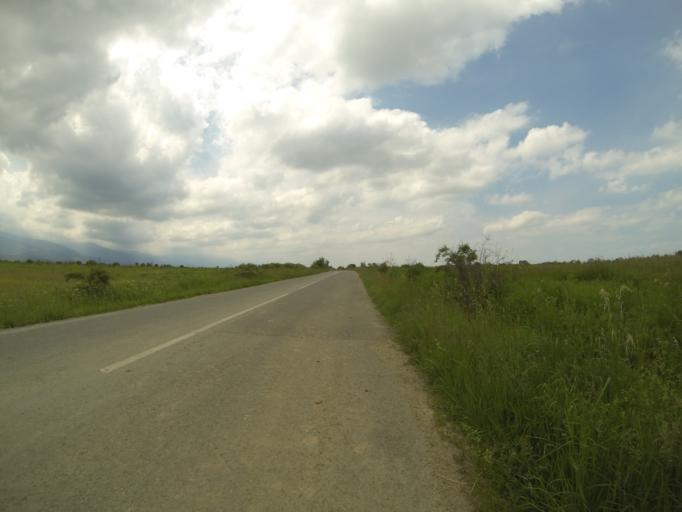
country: RO
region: Brasov
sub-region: Comuna Harseni
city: Harseni
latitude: 45.7360
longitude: 25.0574
